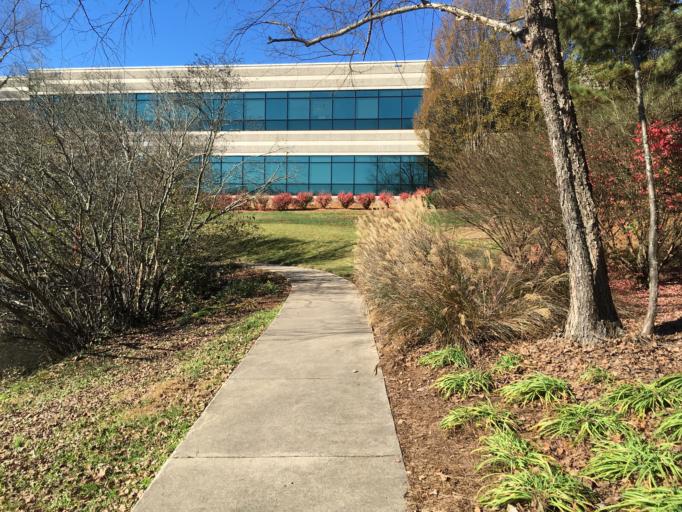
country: US
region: Georgia
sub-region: Fulton County
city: Johns Creek
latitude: 34.0620
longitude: -84.1700
